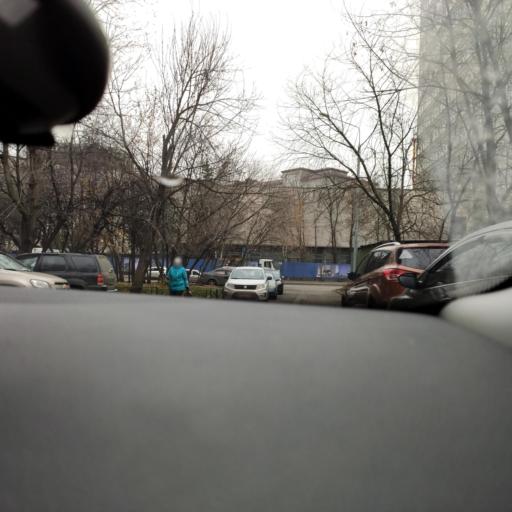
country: RU
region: Moscow
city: Ostankinskiy
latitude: 55.8296
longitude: 37.5991
